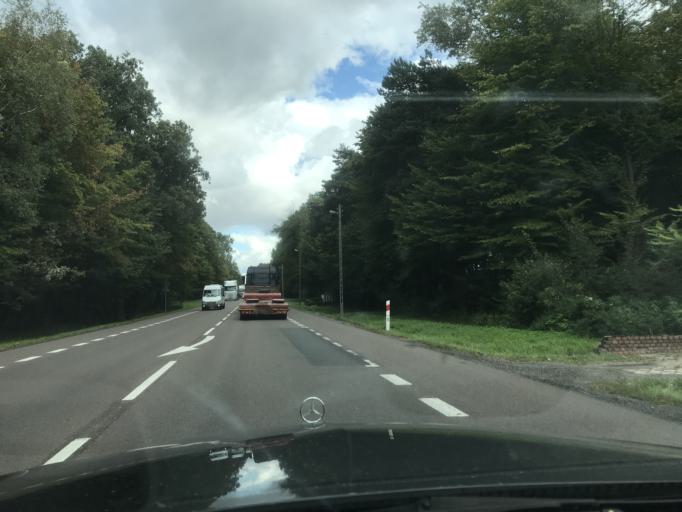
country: PL
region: Lublin Voivodeship
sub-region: Powiat krasnicki
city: Krasnik
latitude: 50.9409
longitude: 22.2685
